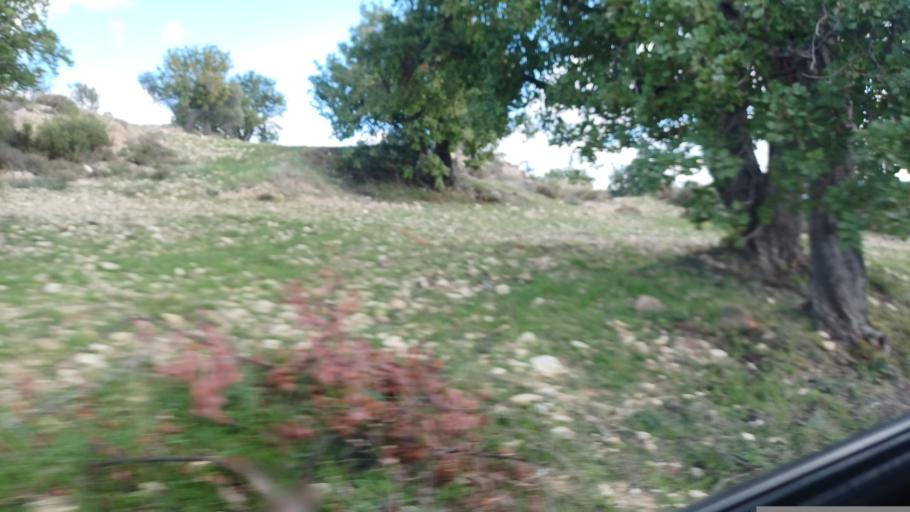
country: CY
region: Limassol
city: Pano Polemidia
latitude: 34.7722
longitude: 32.9773
